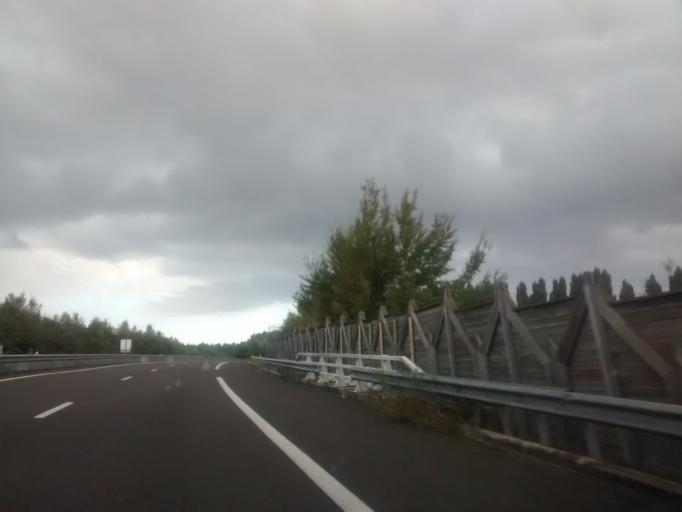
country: FR
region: Brittany
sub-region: Departement d'Ille-et-Vilaine
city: Fouillard
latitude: 48.1509
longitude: -1.5995
